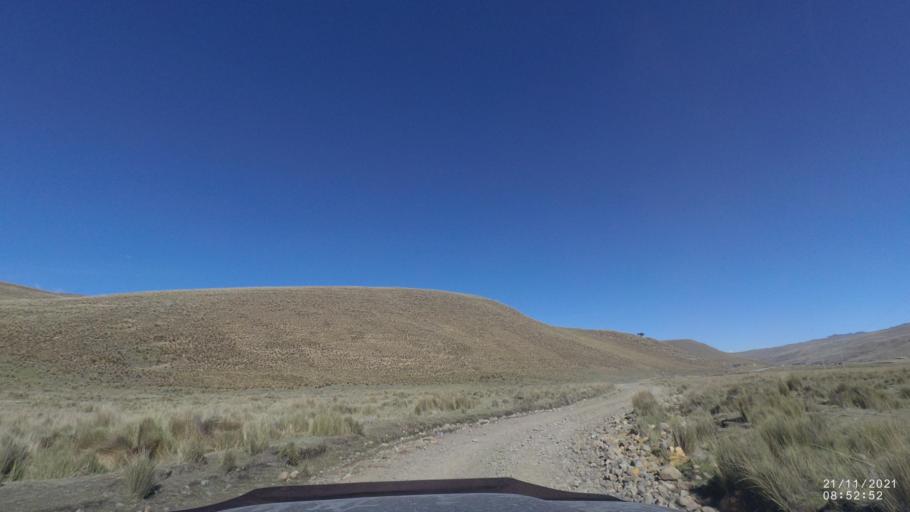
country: BO
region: Cochabamba
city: Cochabamba
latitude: -17.2112
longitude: -66.2398
